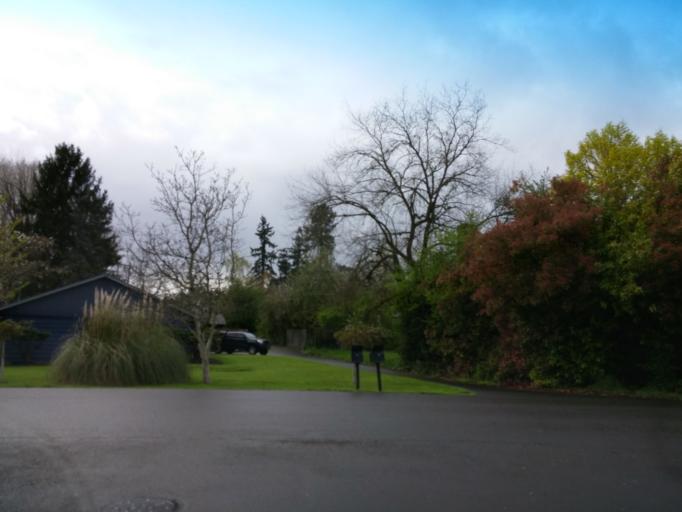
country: US
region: Oregon
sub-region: Washington County
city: Cedar Mill
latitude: 45.5165
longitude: -122.8270
